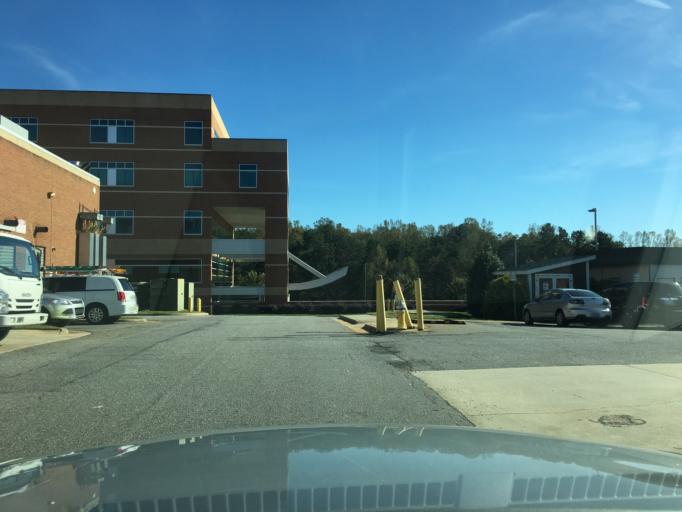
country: US
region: North Carolina
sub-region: Catawba County
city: Conover
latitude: 35.7135
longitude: -81.2684
